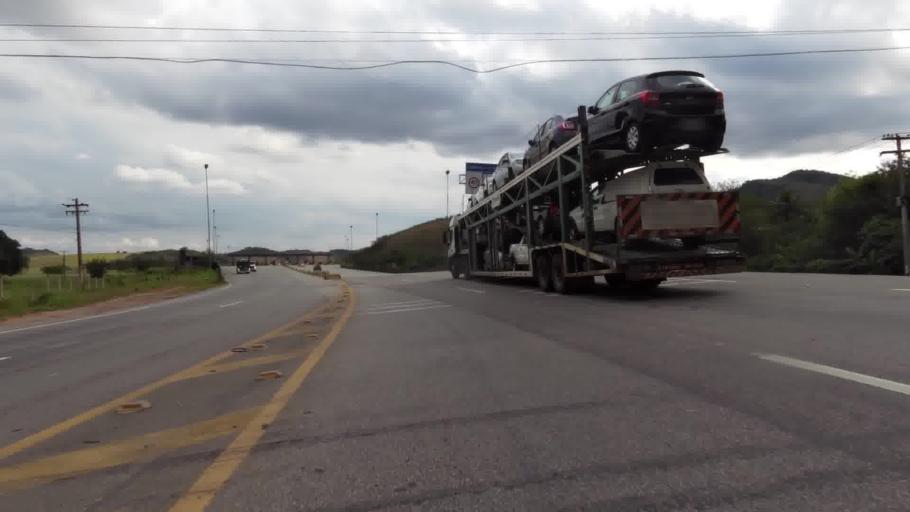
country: BR
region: Rio de Janeiro
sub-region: Casimiro De Abreu
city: Casimiro de Abreu
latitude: -22.4736
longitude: -42.0863
